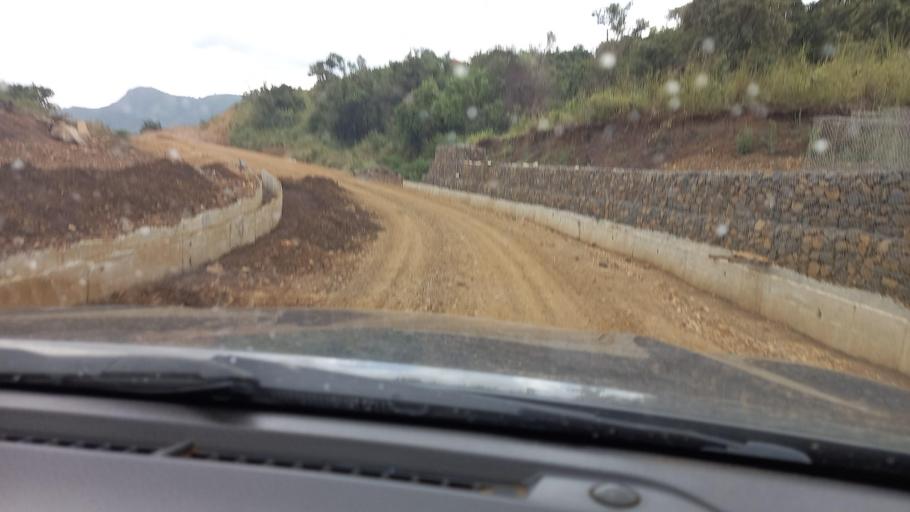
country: ET
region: Southern Nations, Nationalities, and People's Region
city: Mizan Teferi
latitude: 6.2082
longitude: 35.6686
